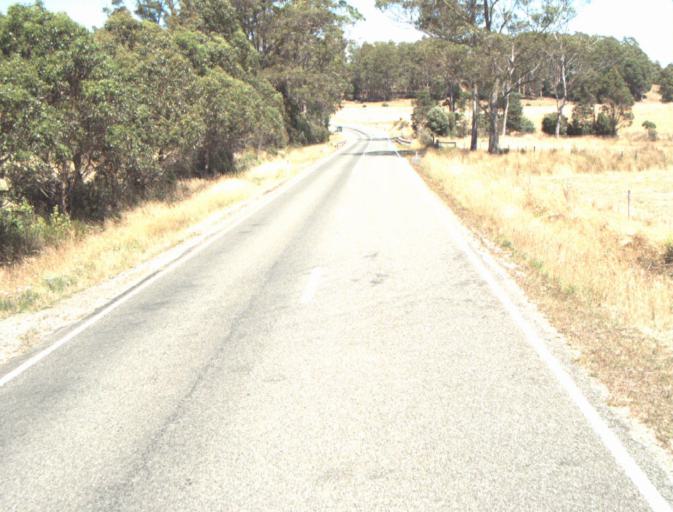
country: AU
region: Tasmania
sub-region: Launceston
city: Newstead
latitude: -41.3307
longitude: 147.3522
